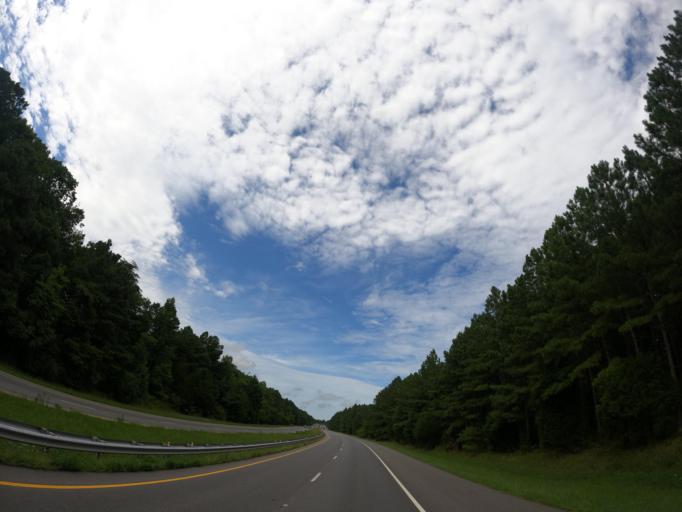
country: US
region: Maryland
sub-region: Calvert County
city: Chesapeake Ranch Estates
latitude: 38.3575
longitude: -76.4536
